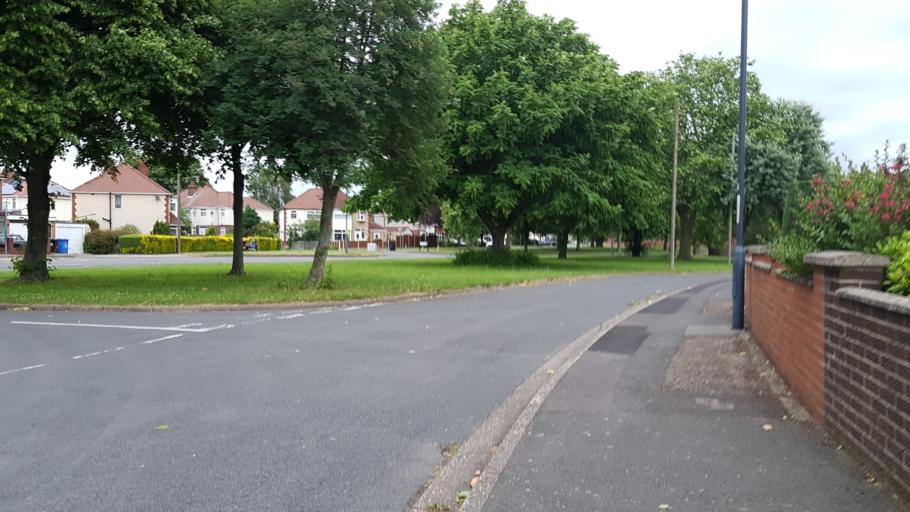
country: GB
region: England
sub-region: Derby
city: Derby
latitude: 52.8874
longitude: -1.4392
